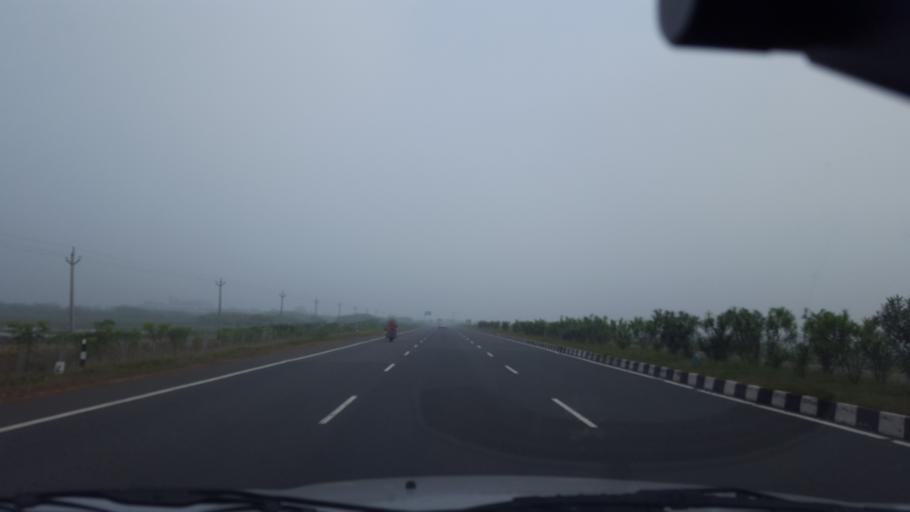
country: IN
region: Andhra Pradesh
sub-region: Prakasam
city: Ongole
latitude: 15.4884
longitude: 80.0644
